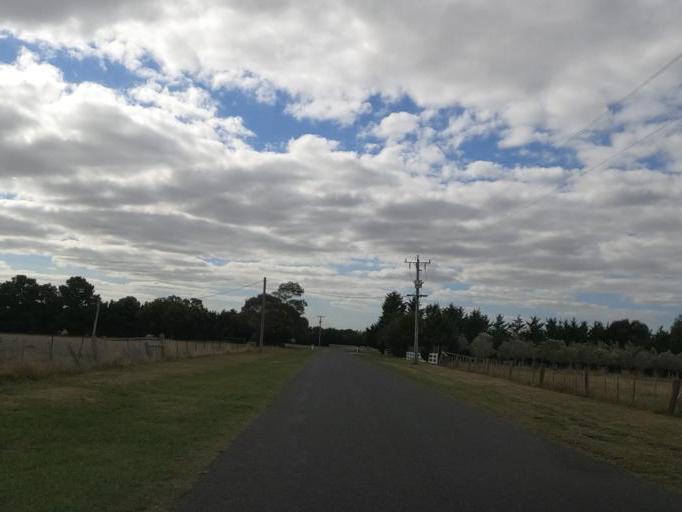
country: AU
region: Victoria
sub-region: Hume
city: Greenvale
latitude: -37.5567
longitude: 144.8703
